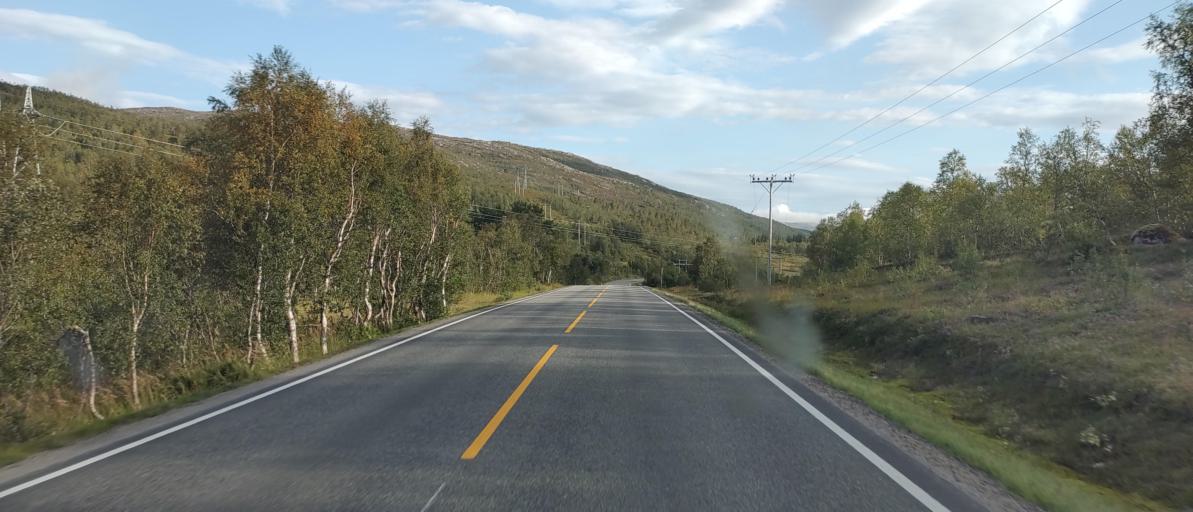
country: NO
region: Nordland
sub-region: Lodingen
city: Lodingen
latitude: 68.5089
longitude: 15.8811
